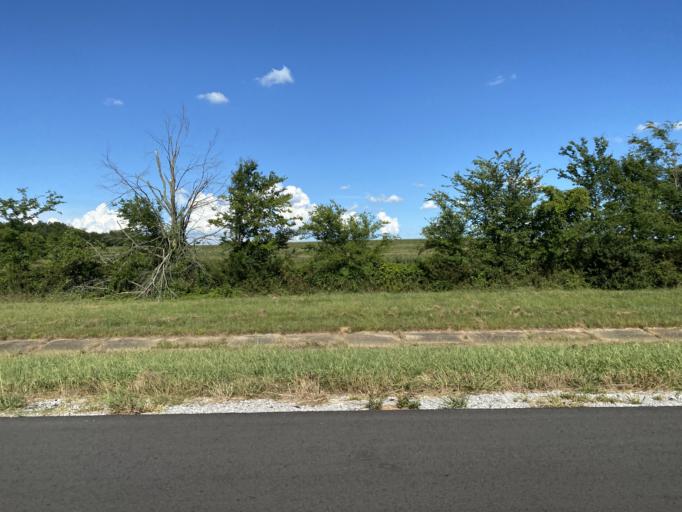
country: US
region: Alabama
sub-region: Limestone County
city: Athens
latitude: 34.7472
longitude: -86.9383
